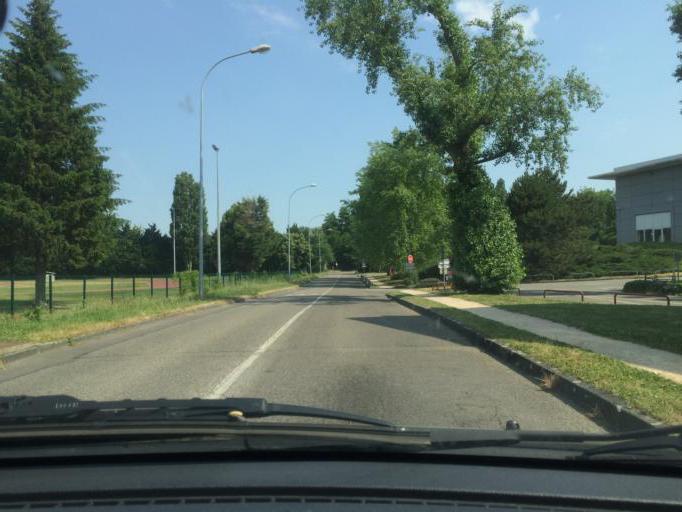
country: FR
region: Rhone-Alpes
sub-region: Departement du Rhone
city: Villeurbanne
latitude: 45.7828
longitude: 4.8649
